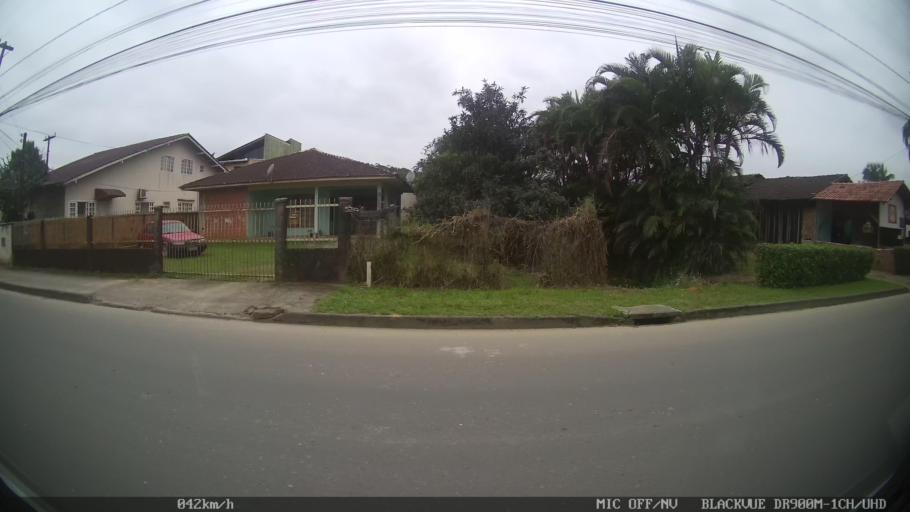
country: BR
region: Santa Catarina
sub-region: Joinville
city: Joinville
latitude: -26.3549
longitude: -48.8278
